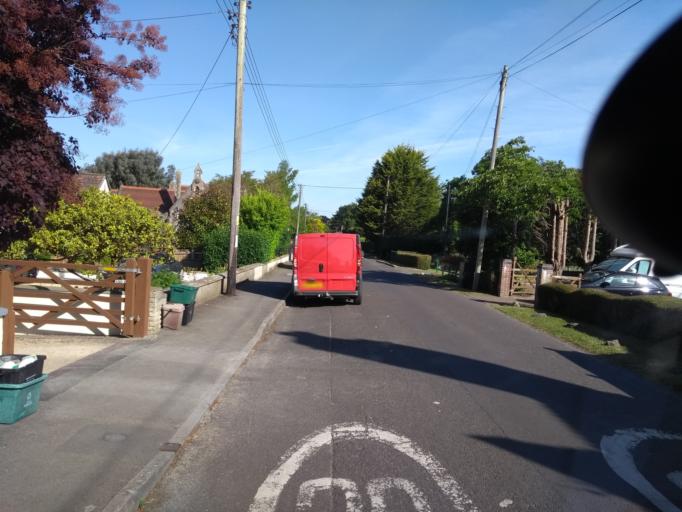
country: GB
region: England
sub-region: Somerset
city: Highbridge
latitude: 51.2496
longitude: -2.9540
